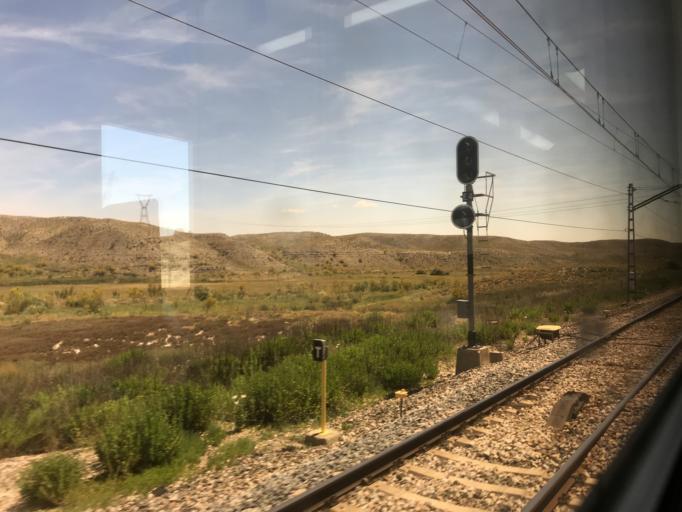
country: ES
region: Madrid
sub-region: Provincia de Madrid
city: Ciempozuelos
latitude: 40.1761
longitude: -3.6304
